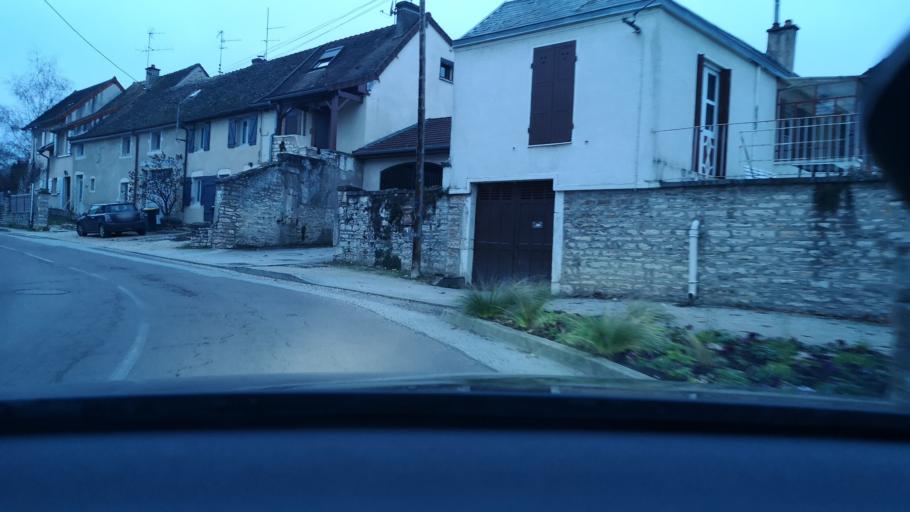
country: FR
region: Bourgogne
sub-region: Departement de Saone-et-Loire
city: Saint-Remy
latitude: 46.7669
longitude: 4.8193
